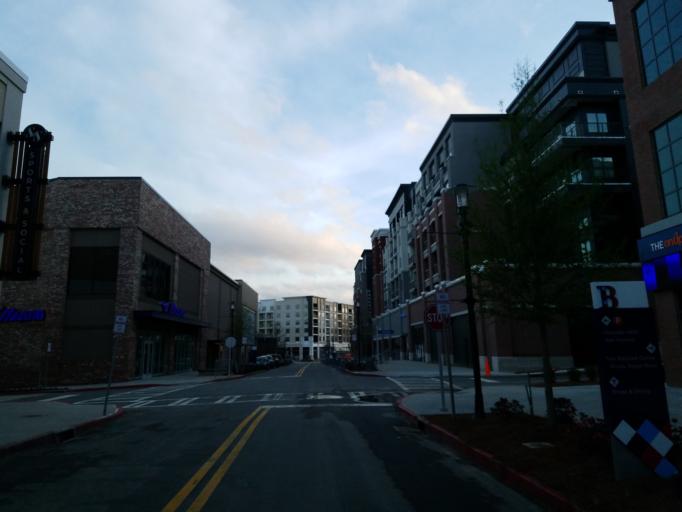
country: US
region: Georgia
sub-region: Cobb County
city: Vinings
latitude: 33.8897
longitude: -84.4696
